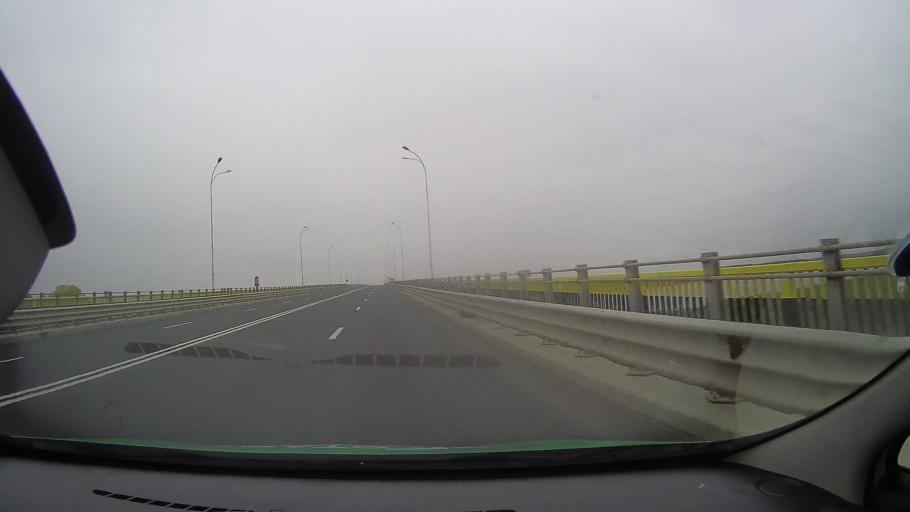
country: RO
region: Ialomita
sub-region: Comuna Giurgeni
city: Giurgeni
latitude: 44.7532
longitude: 27.8837
